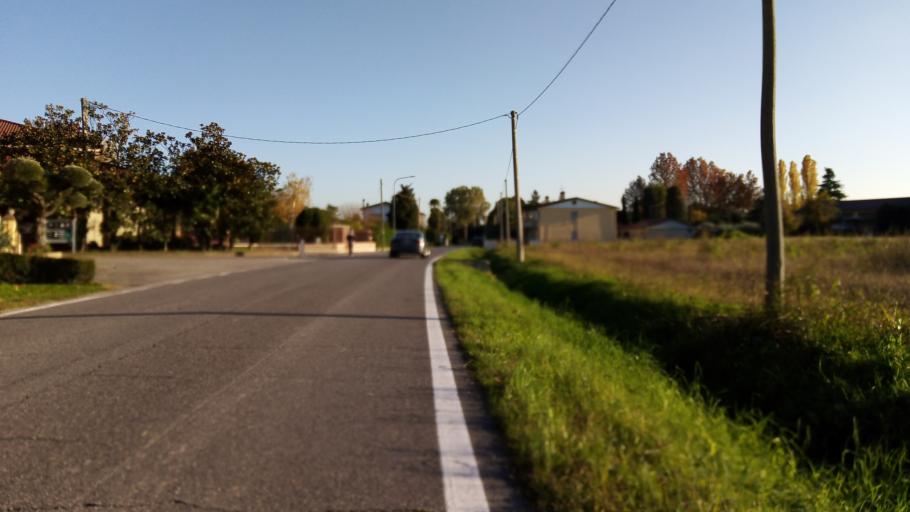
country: IT
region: Veneto
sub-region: Provincia di Padova
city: Abano Terme
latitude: 45.3546
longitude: 11.7984
